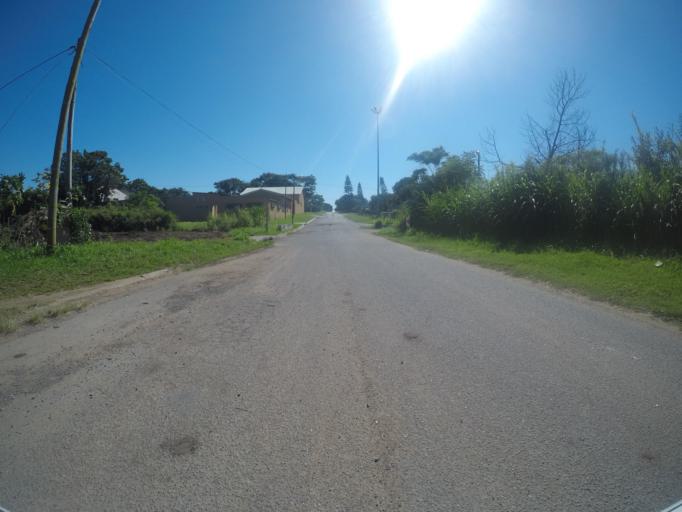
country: ZA
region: Eastern Cape
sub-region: Buffalo City Metropolitan Municipality
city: East London
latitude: -32.9409
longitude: 28.0026
